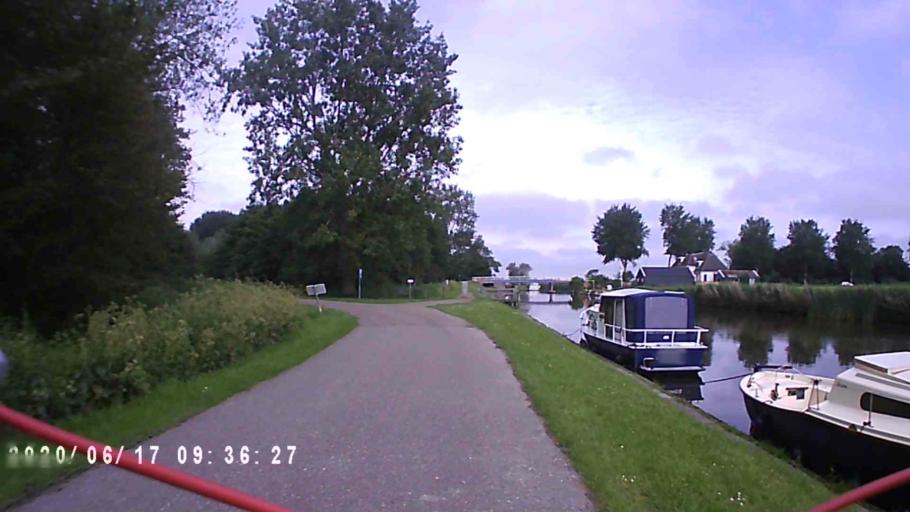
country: NL
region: Groningen
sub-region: Gemeente De Marne
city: Ulrum
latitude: 53.3509
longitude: 6.3713
